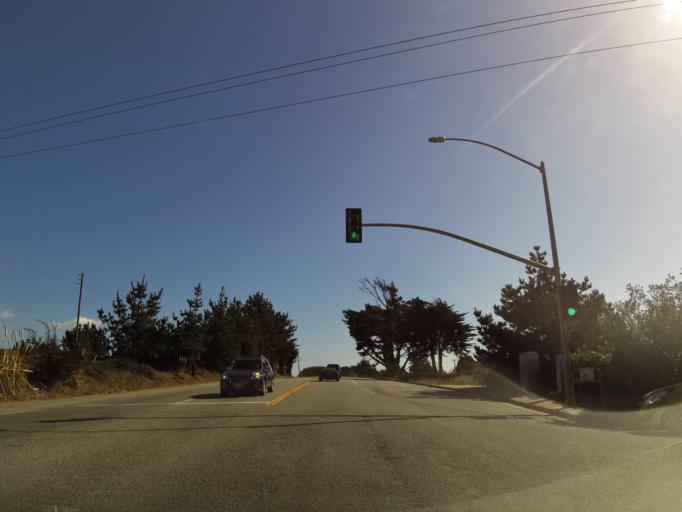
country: US
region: California
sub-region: San Mateo County
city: Colma
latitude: 37.6462
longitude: -122.4710
